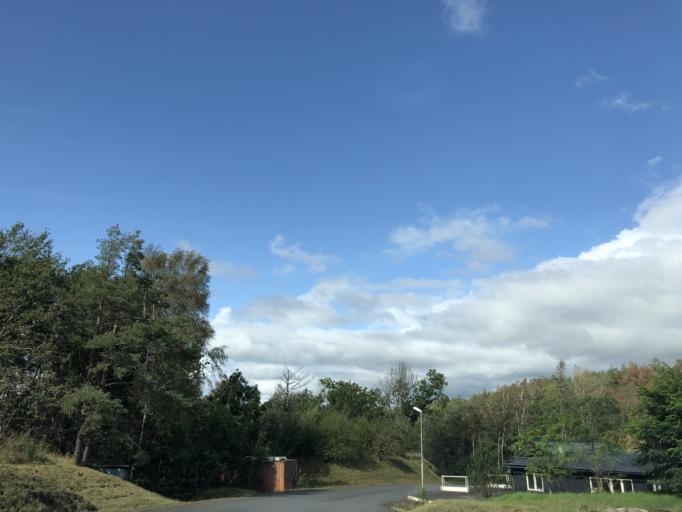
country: SE
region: Vaestra Goetaland
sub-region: Goteborg
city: Majorna
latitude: 57.7138
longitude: 11.8509
